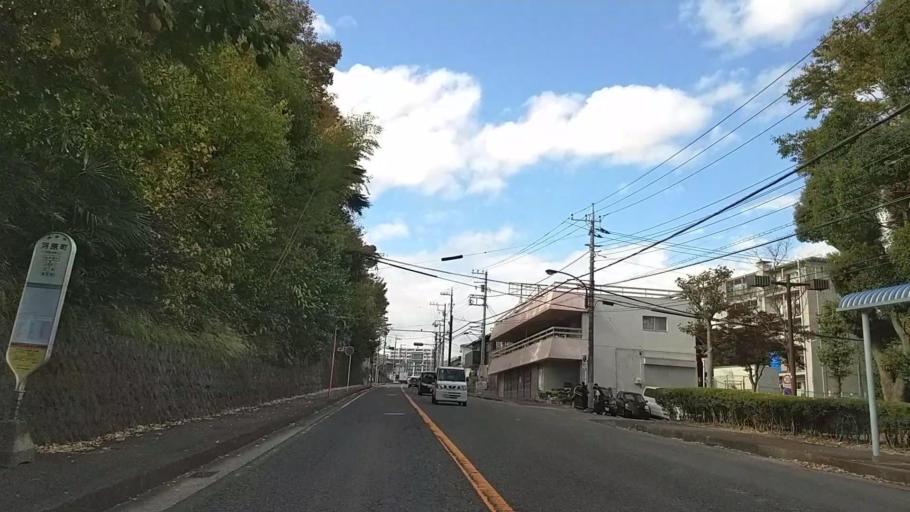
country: JP
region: Kanagawa
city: Hadano
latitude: 35.3692
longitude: 139.2344
